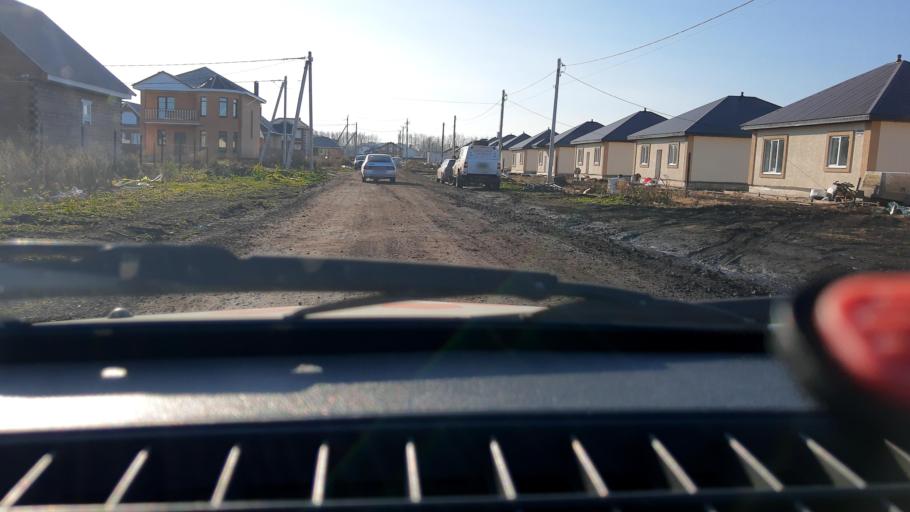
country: RU
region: Bashkortostan
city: Kabakovo
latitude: 54.6282
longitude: 56.1373
